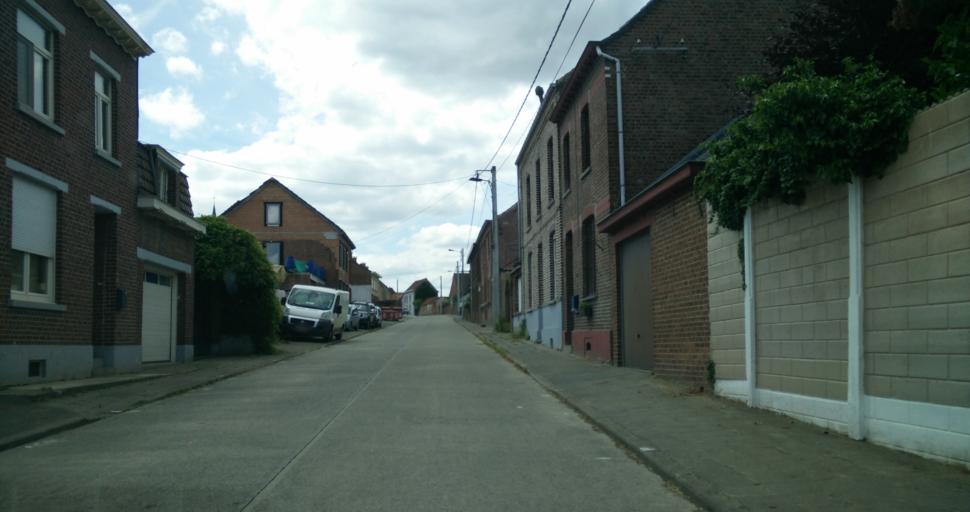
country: BE
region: Wallonia
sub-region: Province du Hainaut
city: Flobecq
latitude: 50.7223
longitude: 3.7835
